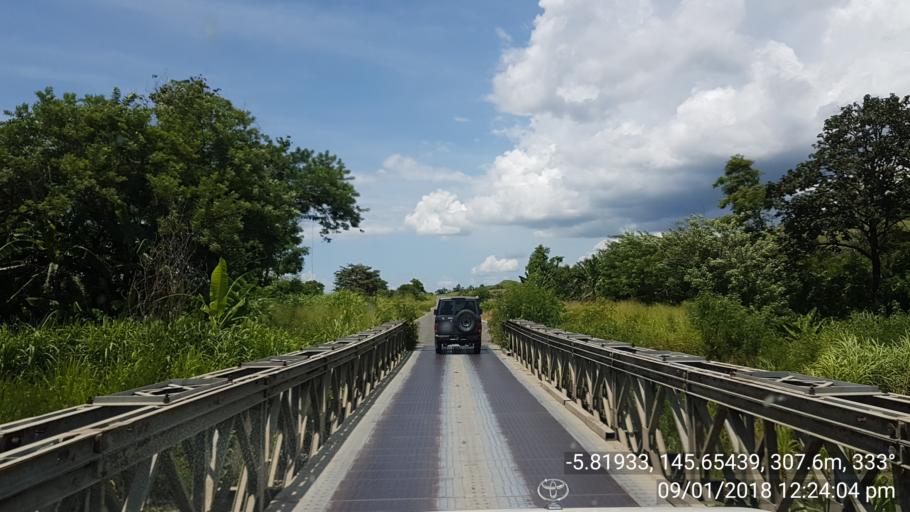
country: PG
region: Eastern Highlands
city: Goroka
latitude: -5.8194
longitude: 145.6544
